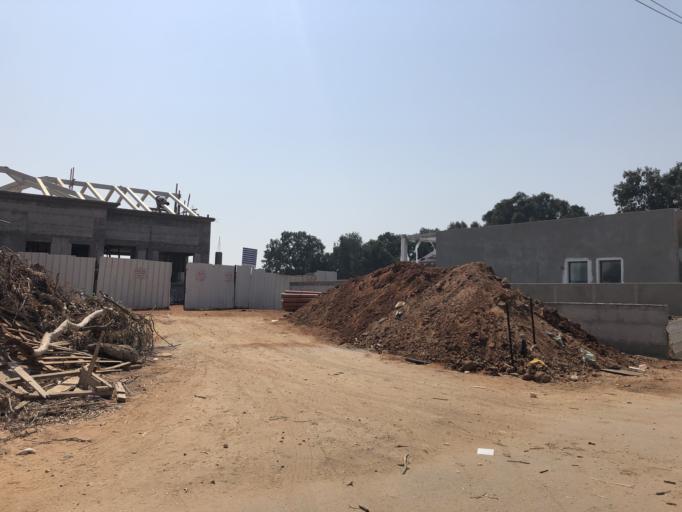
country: IL
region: Tel Aviv
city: Giv`atayim
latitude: 32.0559
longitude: 34.8311
